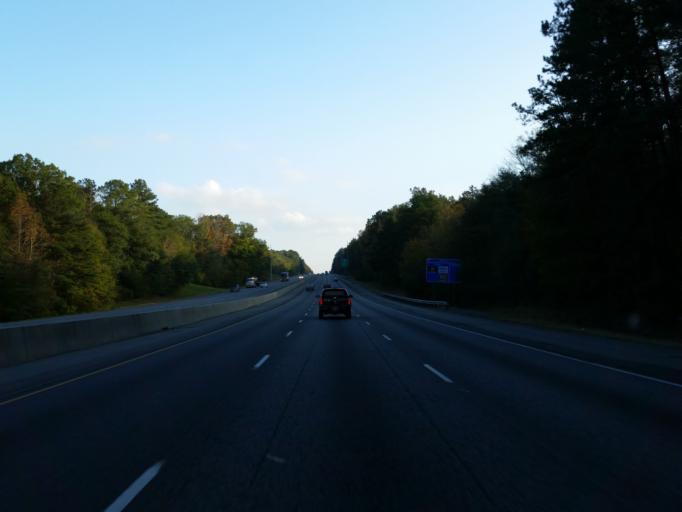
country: US
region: Georgia
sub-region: Bibb County
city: West Point
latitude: 32.8531
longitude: -83.7426
